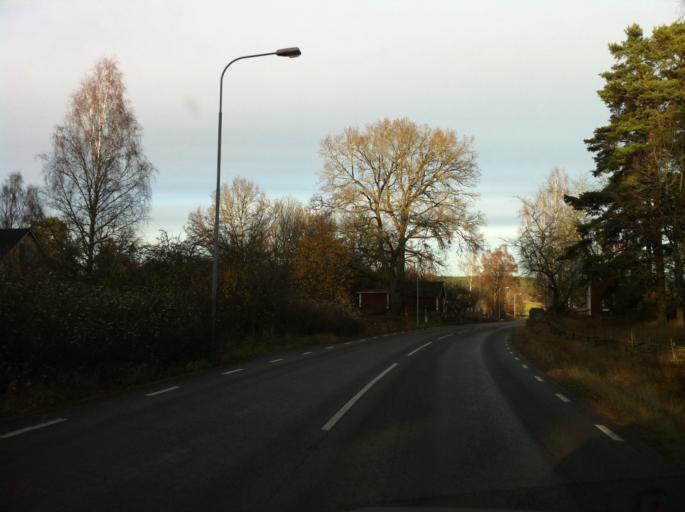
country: SE
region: Kalmar
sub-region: Hultsfreds Kommun
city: Virserum
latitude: 57.3974
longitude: 15.6039
